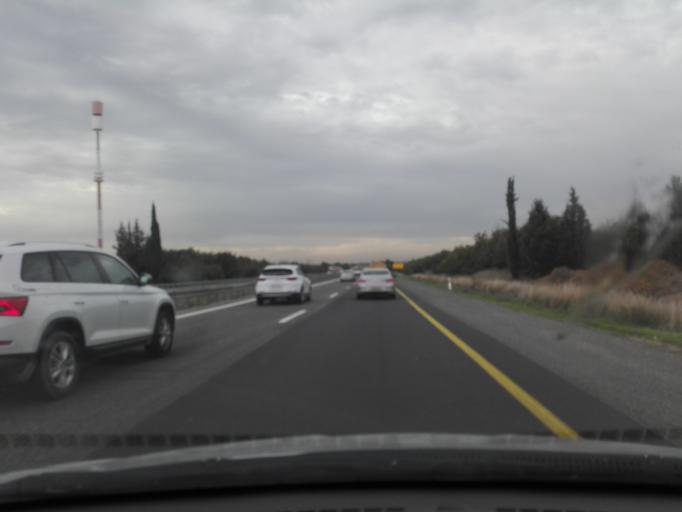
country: IL
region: Central District
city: Mazkeret Batya
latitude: 31.8659
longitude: 34.8736
